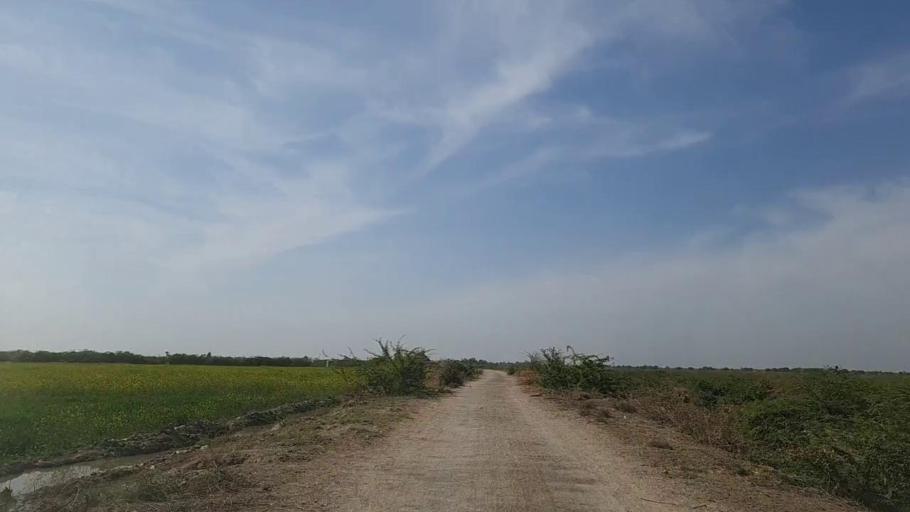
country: PK
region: Sindh
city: Samaro
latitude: 25.2066
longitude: 69.4466
